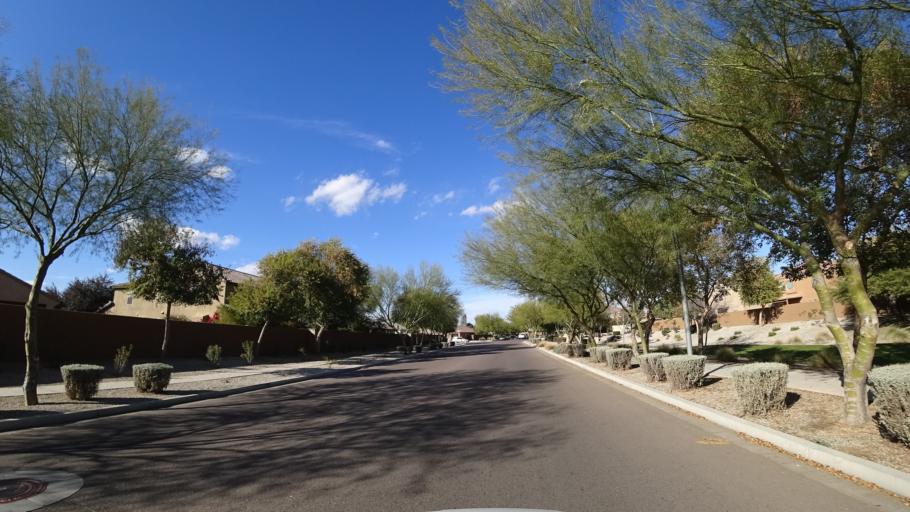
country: US
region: Arizona
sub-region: Maricopa County
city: Tolleson
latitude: 33.4172
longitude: -112.2521
